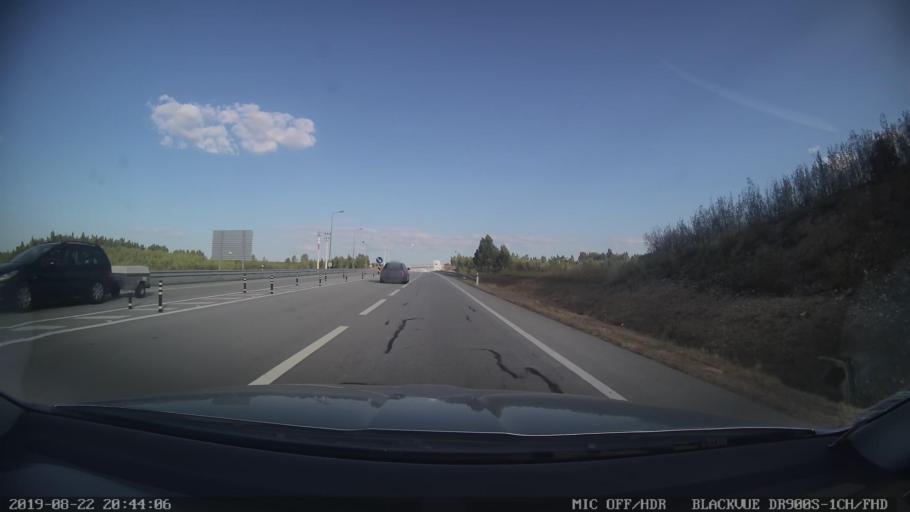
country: PT
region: Castelo Branco
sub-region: Proenca-A-Nova
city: Proenca-a-Nova
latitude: 39.7044
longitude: -7.8451
